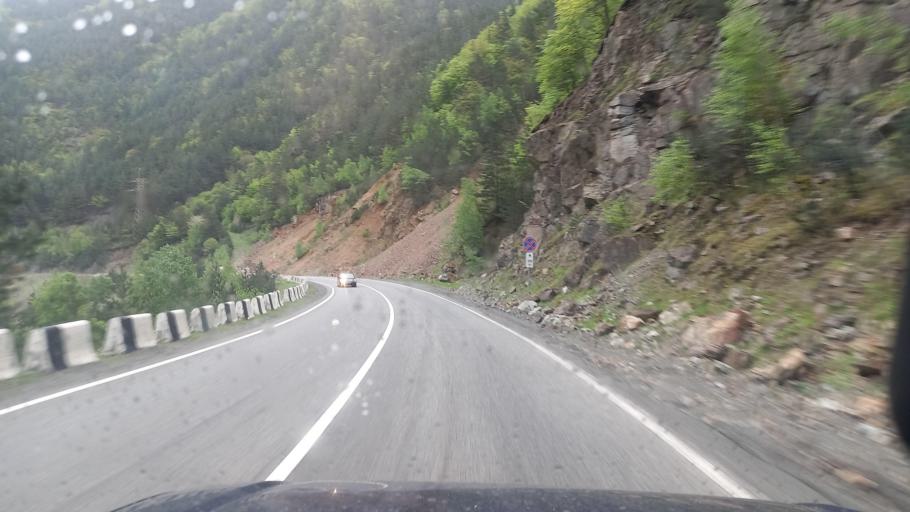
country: RU
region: North Ossetia
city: Mizur
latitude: 42.8095
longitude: 44.0214
